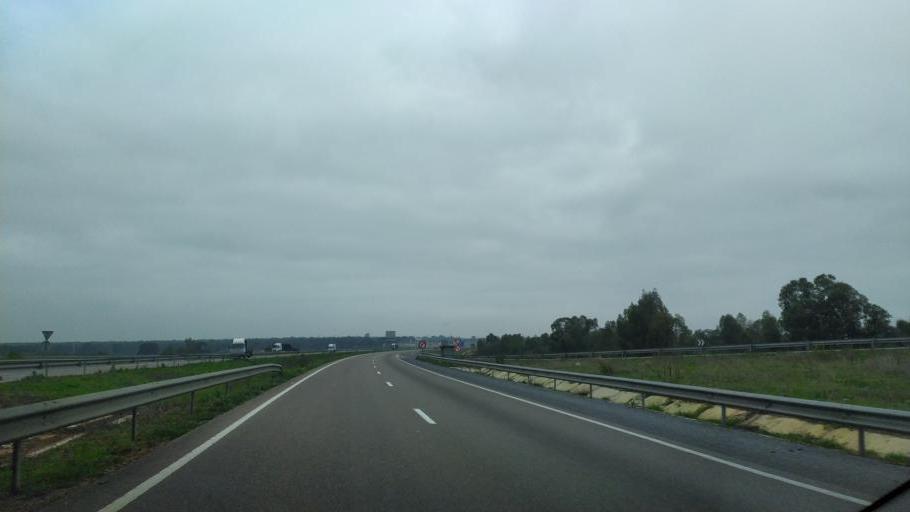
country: MA
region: Rabat-Sale-Zemmour-Zaer
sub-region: Skhirate-Temara
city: Temara
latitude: 33.8462
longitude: -6.8991
